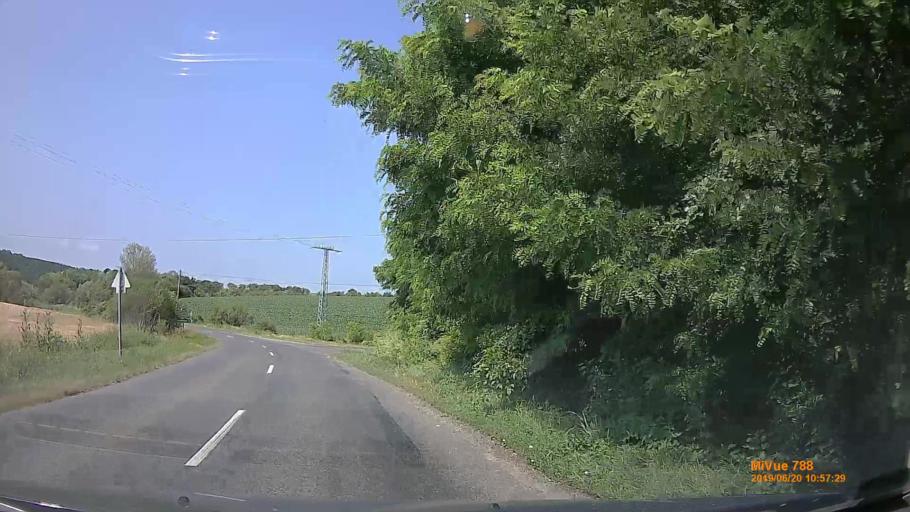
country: HU
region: Baranya
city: Mecseknadasd
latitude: 46.1535
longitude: 18.5206
